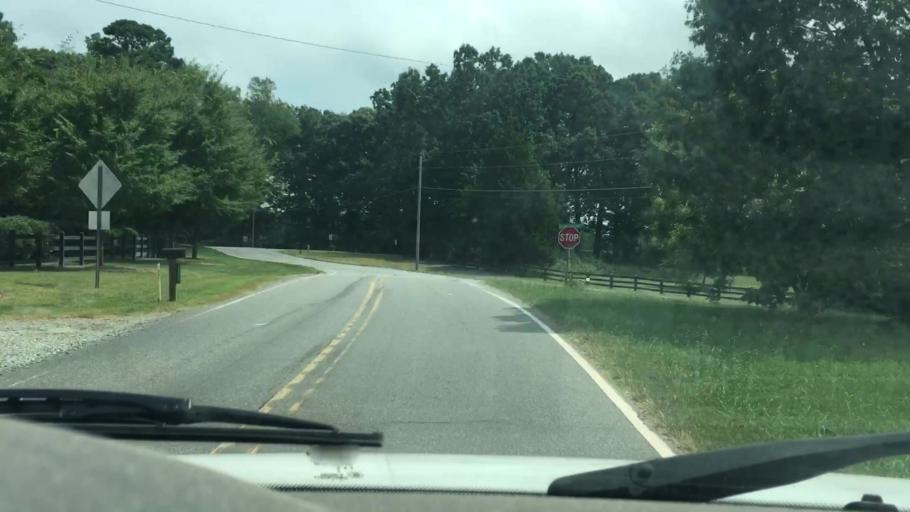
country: US
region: North Carolina
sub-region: Gaston County
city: Davidson
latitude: 35.5077
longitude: -80.7976
